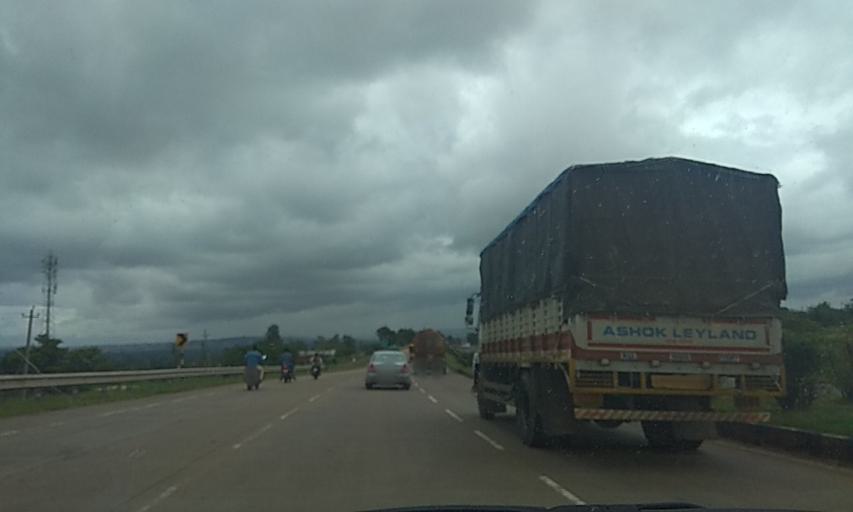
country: IN
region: Karnataka
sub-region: Belgaum
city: Belgaum
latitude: 15.8114
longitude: 74.5676
